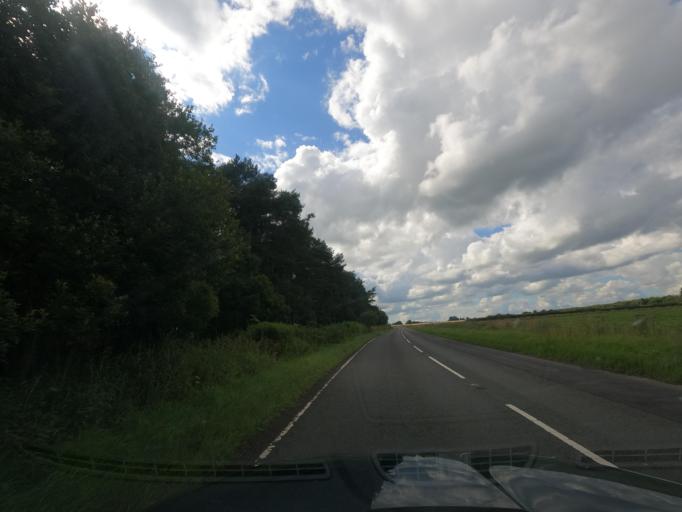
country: GB
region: Scotland
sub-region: The Scottish Borders
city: Earlston
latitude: 55.7152
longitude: -2.5689
